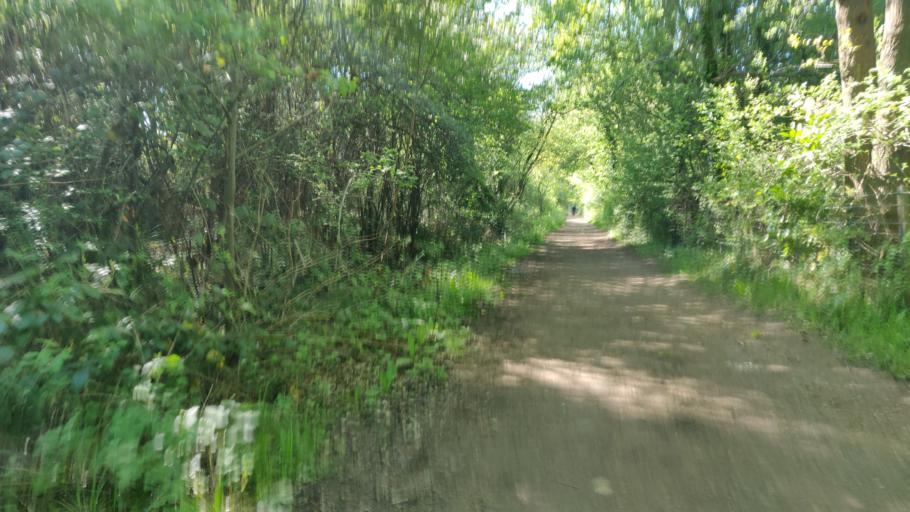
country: GB
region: England
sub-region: West Sussex
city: Rudgwick
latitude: 51.0642
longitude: -0.4002
